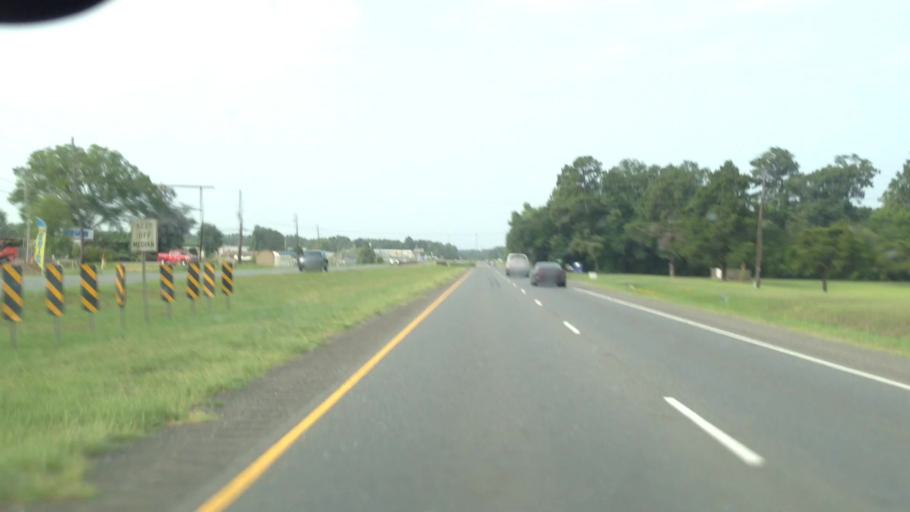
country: US
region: Louisiana
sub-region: De Soto Parish
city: Stonewall
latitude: 32.3711
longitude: -93.8236
